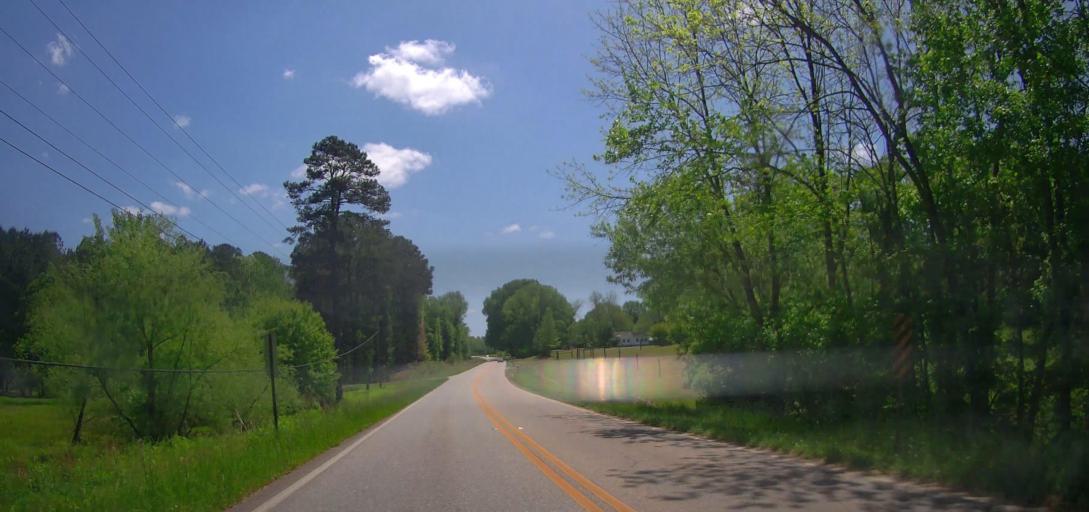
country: US
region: Georgia
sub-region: Jones County
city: Gray
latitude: 33.0299
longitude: -83.5782
